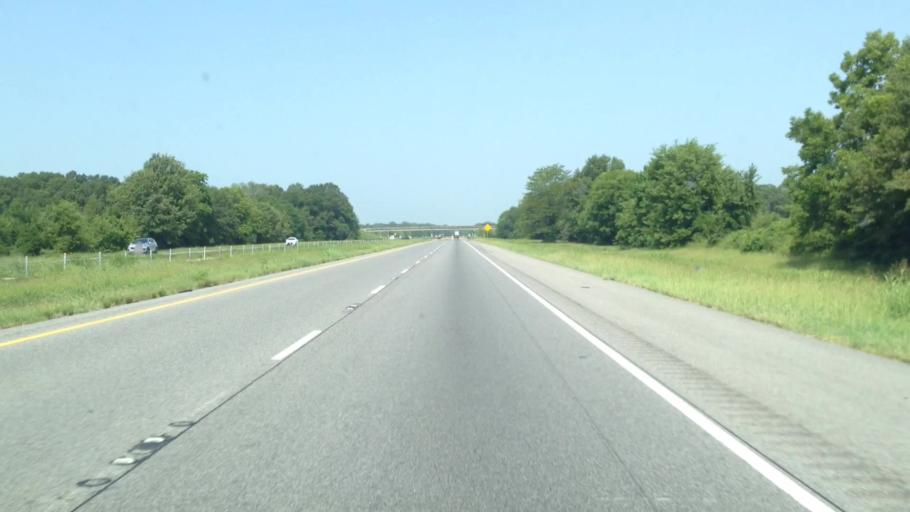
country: US
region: Louisiana
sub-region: Richland Parish
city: Delhi
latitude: 32.4243
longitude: -91.3626
